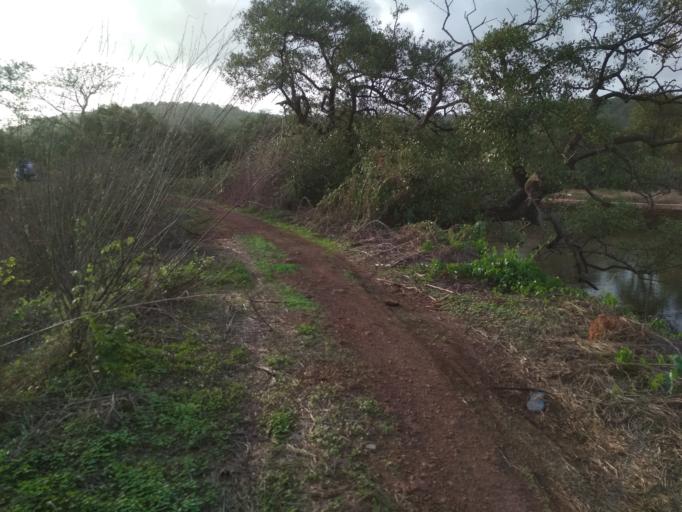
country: IN
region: Goa
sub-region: North Goa
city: Serula
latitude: 15.5291
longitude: 73.8617
